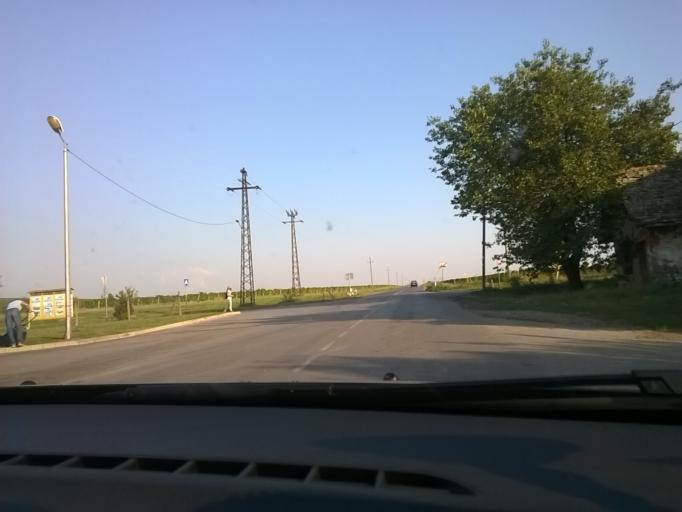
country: RS
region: Autonomna Pokrajina Vojvodina
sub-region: Juznobanatski Okrug
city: Vrsac
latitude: 45.1100
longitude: 21.3106
